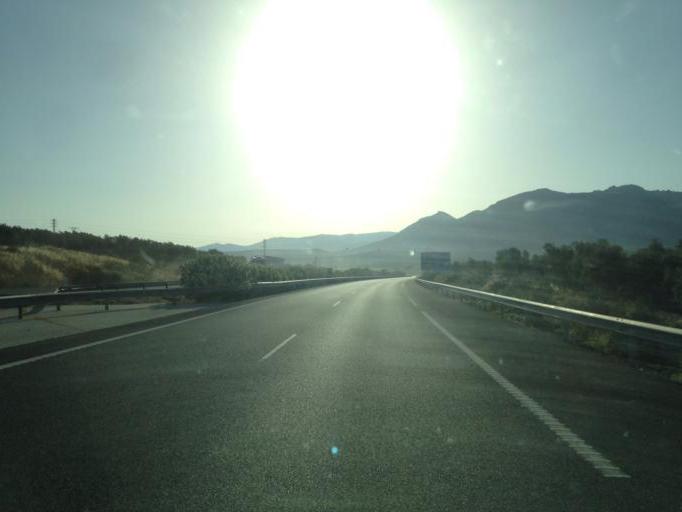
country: ES
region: Andalusia
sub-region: Provincia de Malaga
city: Villanueva del Trabuco
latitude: 37.0654
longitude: -4.3387
